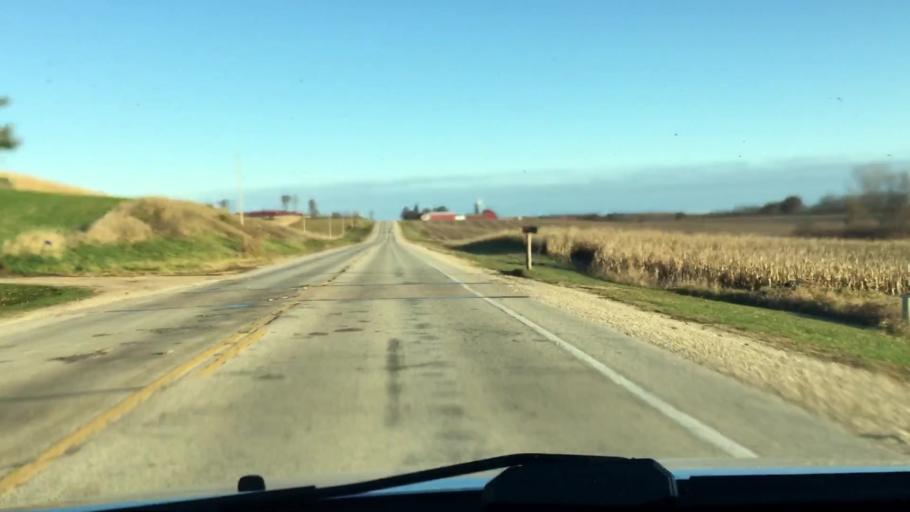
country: US
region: Wisconsin
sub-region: Dodge County
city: Theresa
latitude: 43.4189
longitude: -88.4502
